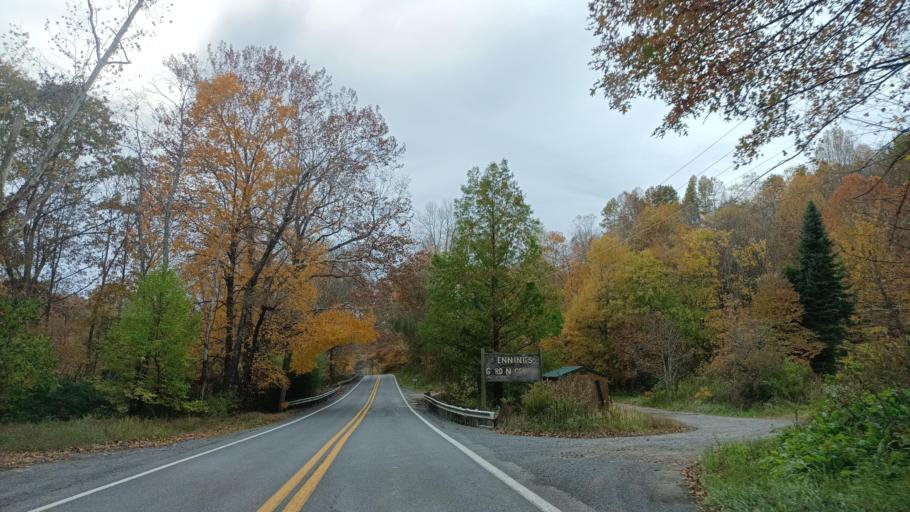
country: US
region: West Virginia
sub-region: Taylor County
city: Grafton
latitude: 39.3350
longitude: -79.8757
